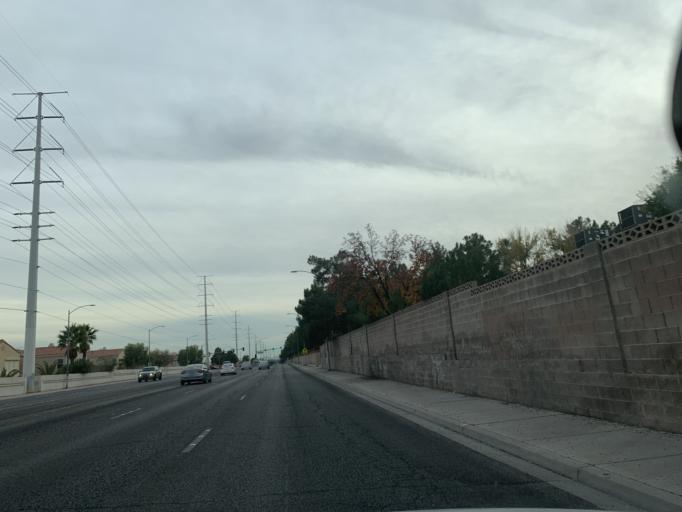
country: US
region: Nevada
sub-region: Clark County
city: Spring Valley
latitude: 36.1534
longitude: -115.2798
